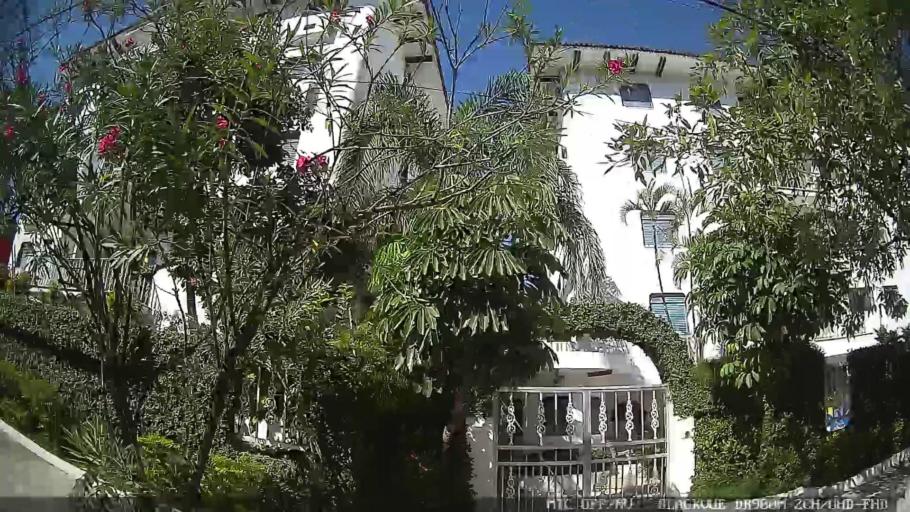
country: BR
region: Sao Paulo
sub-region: Guaruja
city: Guaruja
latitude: -23.9917
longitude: -46.2407
